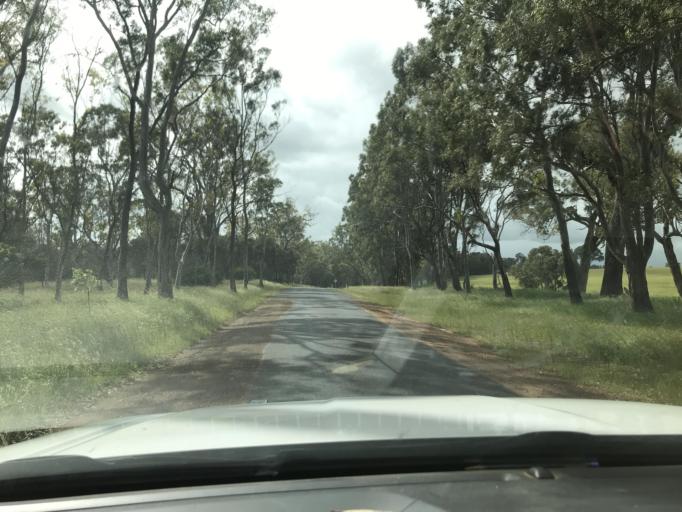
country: AU
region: South Australia
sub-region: Wattle Range
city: Penola
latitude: -37.1690
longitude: 141.4262
